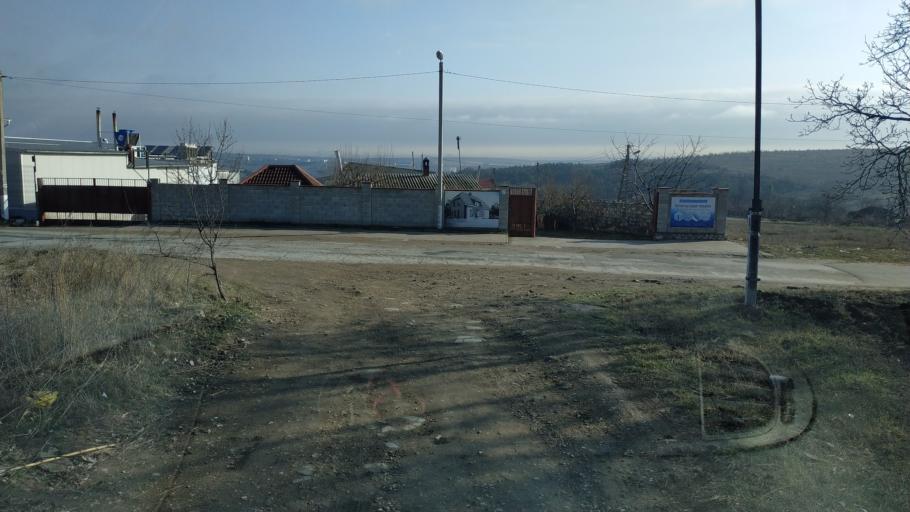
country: MD
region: Laloveni
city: Ialoveni
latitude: 46.9449
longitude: 28.7221
